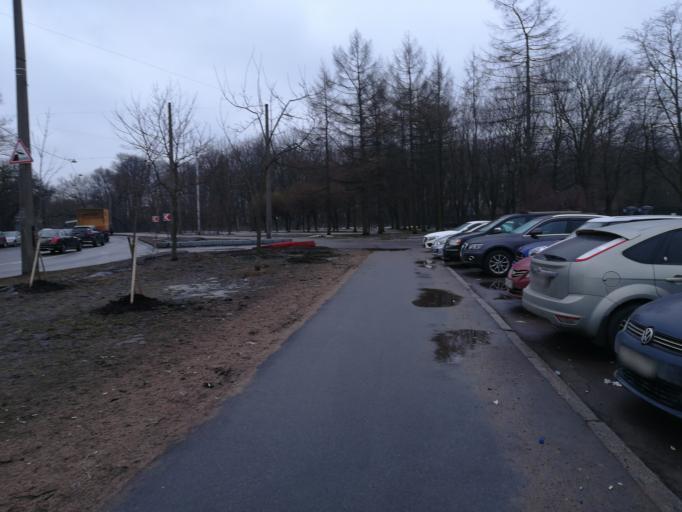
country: RU
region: St.-Petersburg
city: Vasyl'evsky Ostrov
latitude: 59.9486
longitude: 30.2488
